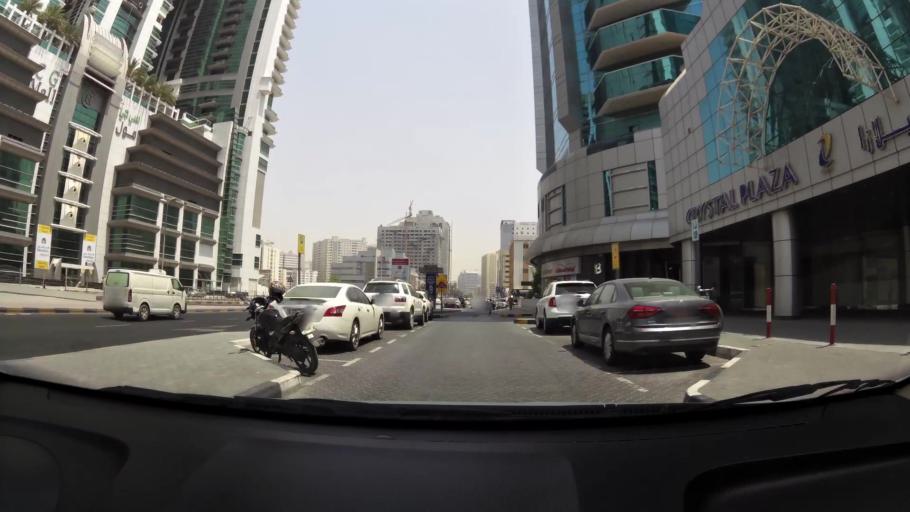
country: AE
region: Ash Shariqah
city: Sharjah
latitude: 25.3448
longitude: 55.3867
